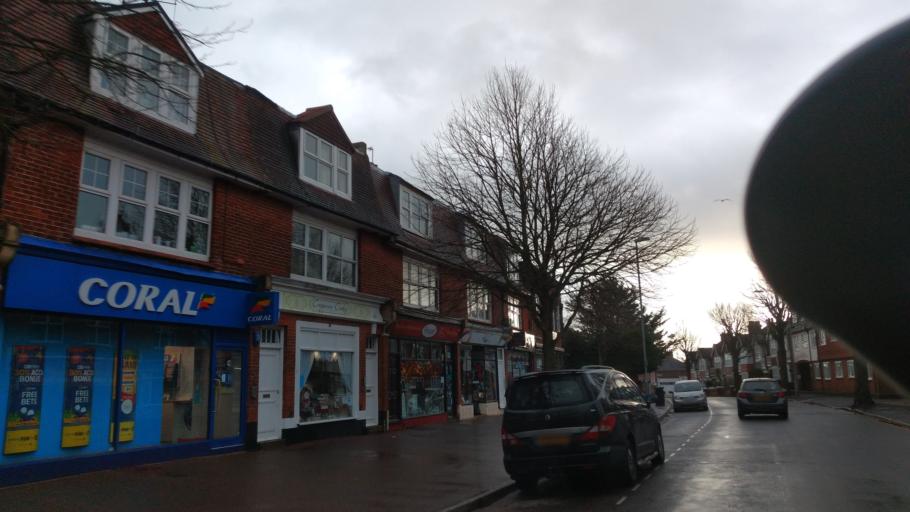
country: GB
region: England
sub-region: East Sussex
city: Eastbourne
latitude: 50.7773
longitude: 0.2566
